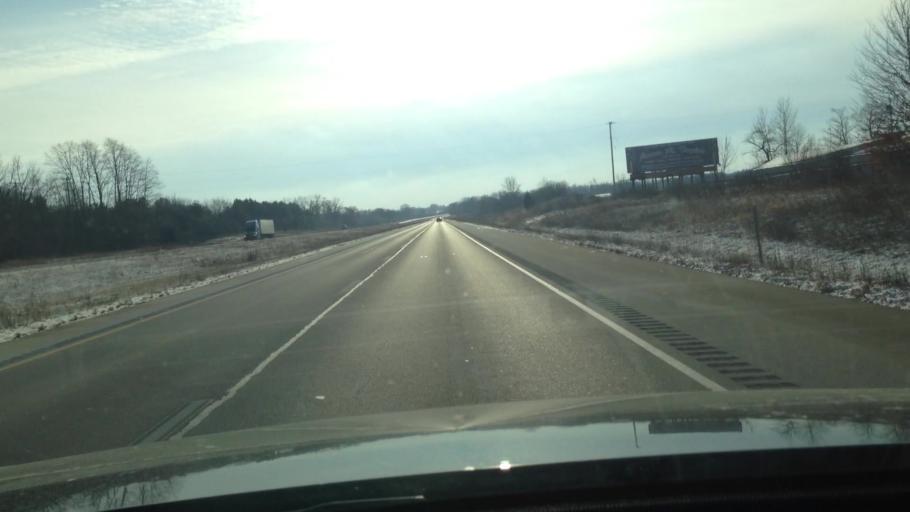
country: US
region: Wisconsin
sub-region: Walworth County
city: Potter Lake
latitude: 42.8194
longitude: -88.3608
